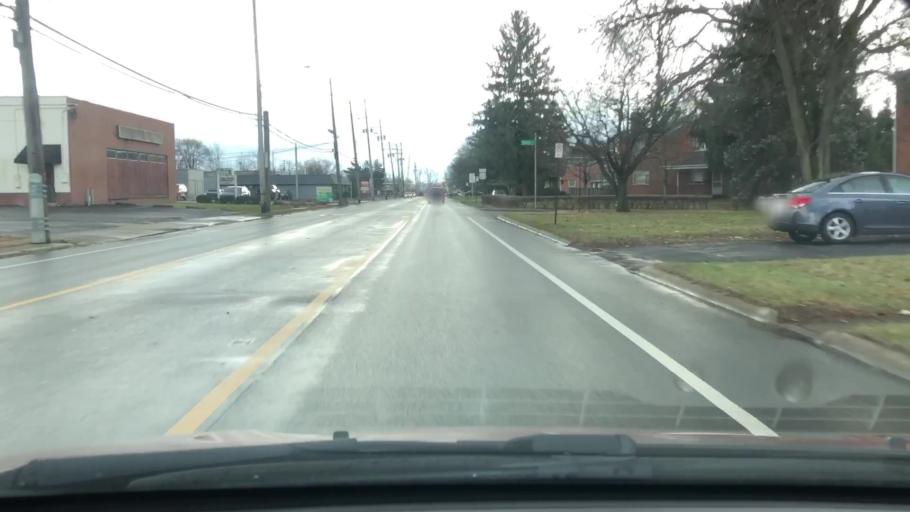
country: US
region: Ohio
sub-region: Franklin County
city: Worthington
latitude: 40.0516
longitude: -83.0001
